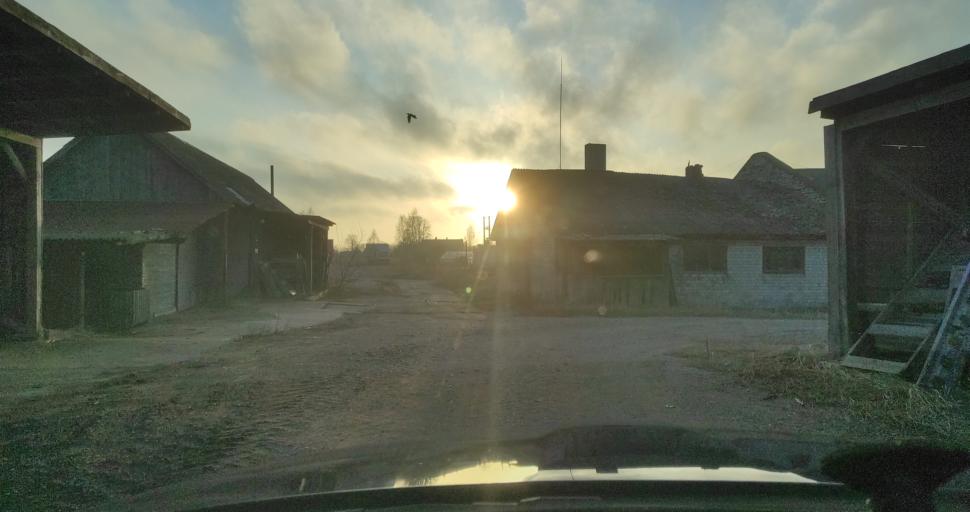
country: LV
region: Aizpute
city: Aizpute
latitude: 56.7996
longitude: 21.7963
